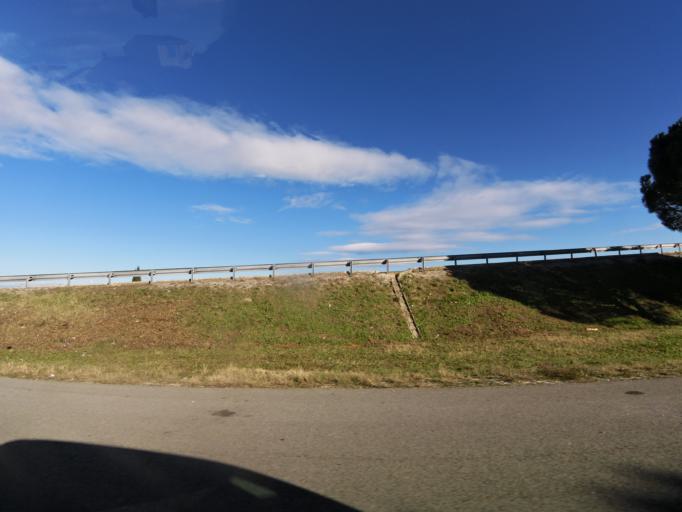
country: FR
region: Languedoc-Roussillon
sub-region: Departement du Gard
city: Milhaud
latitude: 43.7934
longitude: 4.3191
